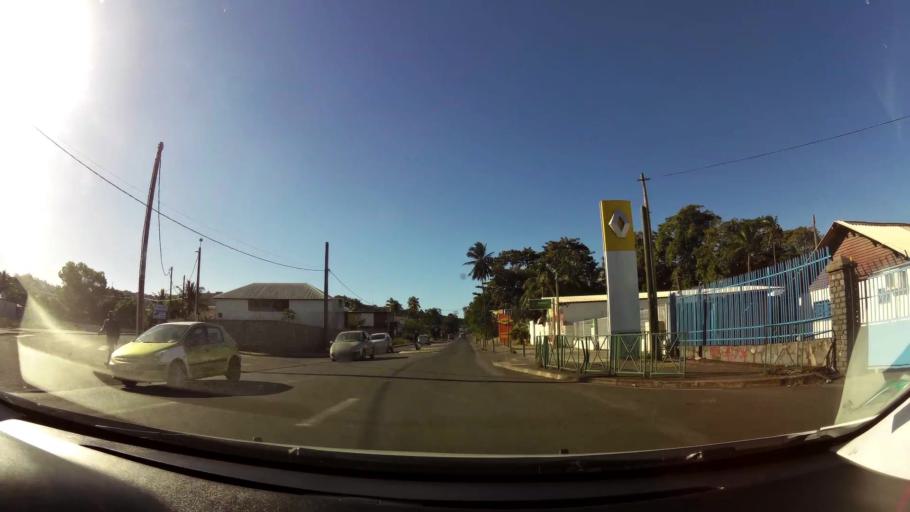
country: YT
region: Mamoudzou
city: Mamoudzou
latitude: -12.7672
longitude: 45.2247
